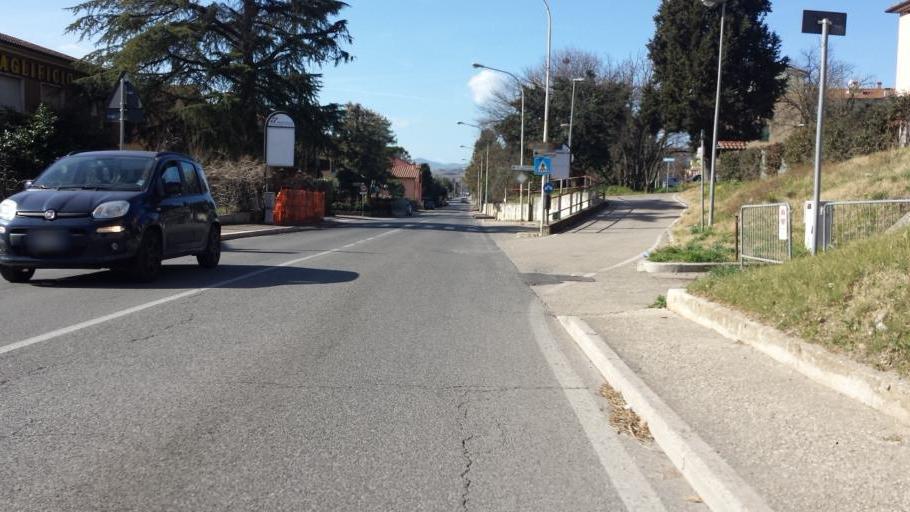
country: IT
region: Umbria
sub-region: Provincia di Terni
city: San Gemini
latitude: 42.5903
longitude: 12.5809
